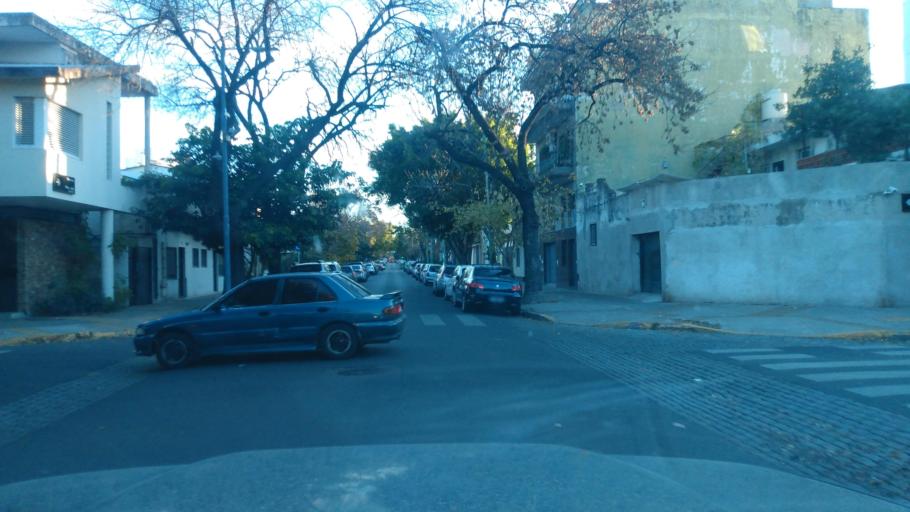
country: AR
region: Buenos Aires F.D.
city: Villa Santa Rita
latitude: -34.5838
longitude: -58.4853
